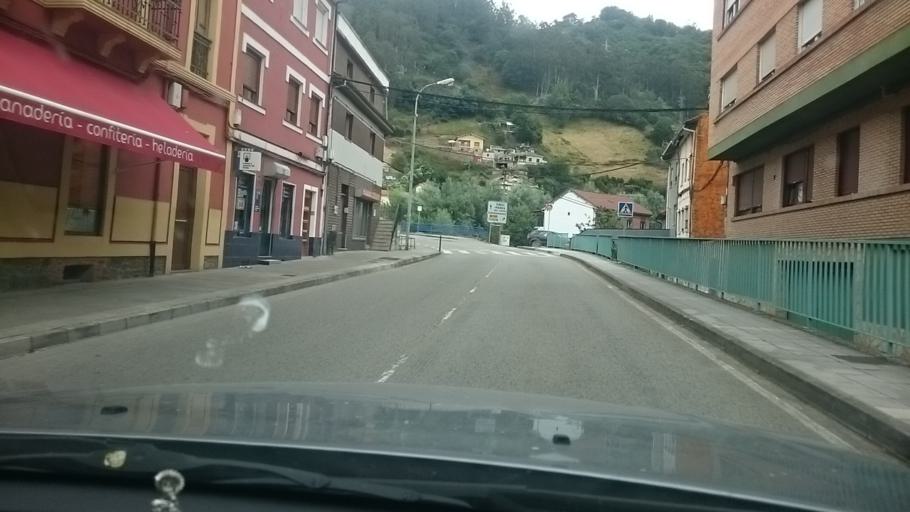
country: ES
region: Asturias
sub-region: Province of Asturias
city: Mieres
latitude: 43.2101
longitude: -5.7827
